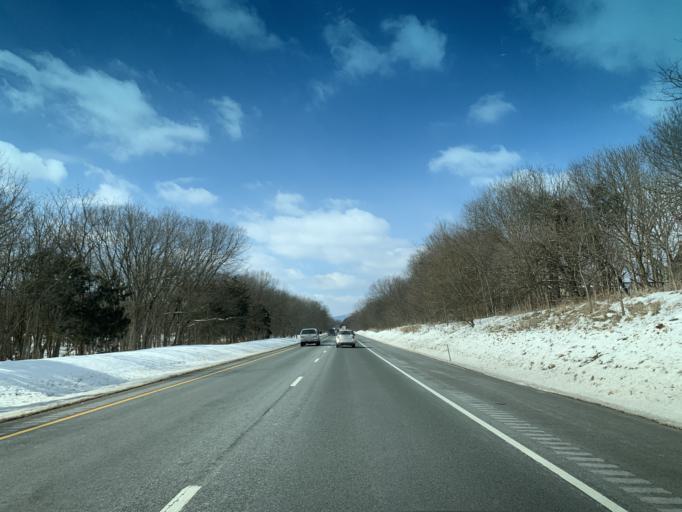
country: US
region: Maryland
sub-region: Washington County
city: Wilson-Conococheague
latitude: 39.6513
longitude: -77.8581
